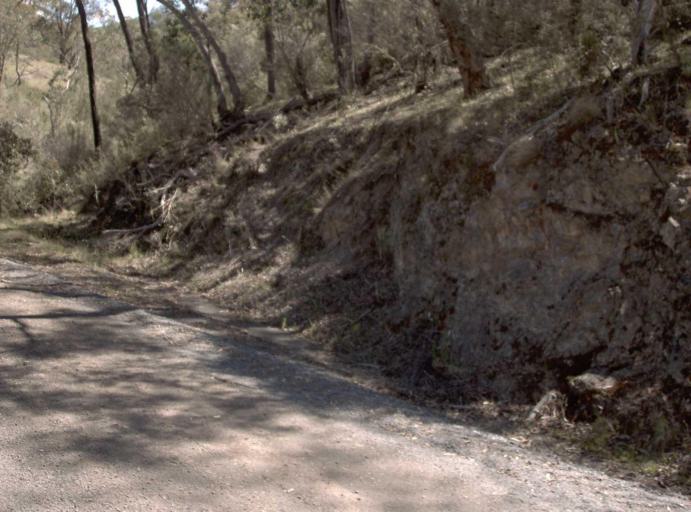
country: AU
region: New South Wales
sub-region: Bombala
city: Bombala
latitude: -37.1025
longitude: 148.6360
